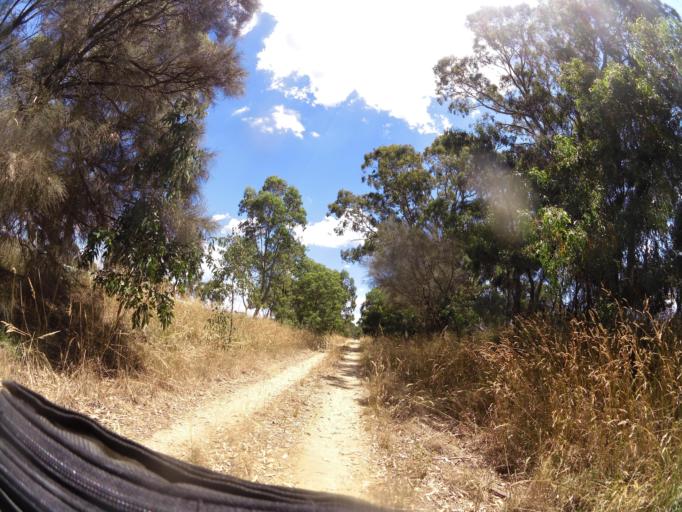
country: AU
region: Victoria
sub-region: Wellington
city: Heyfield
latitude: -37.9828
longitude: 146.8170
